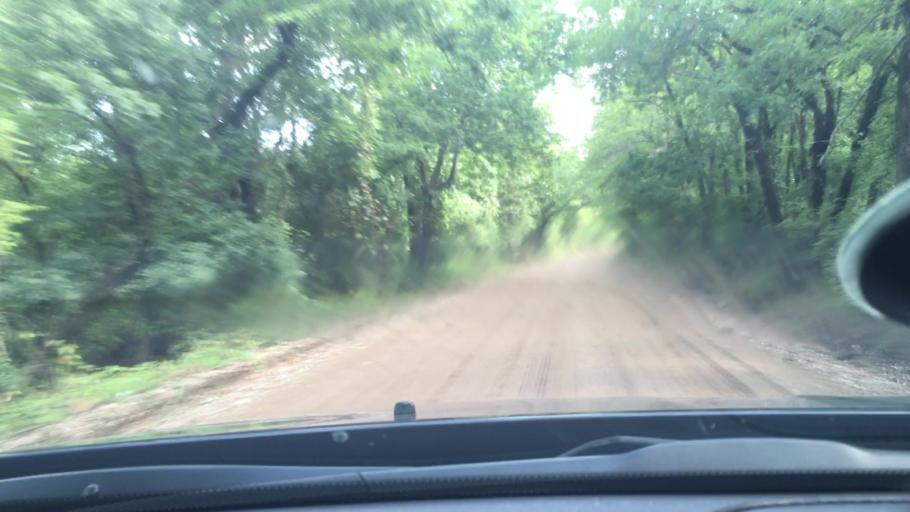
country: US
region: Oklahoma
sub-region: Atoka County
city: Atoka
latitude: 34.4504
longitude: -96.0671
